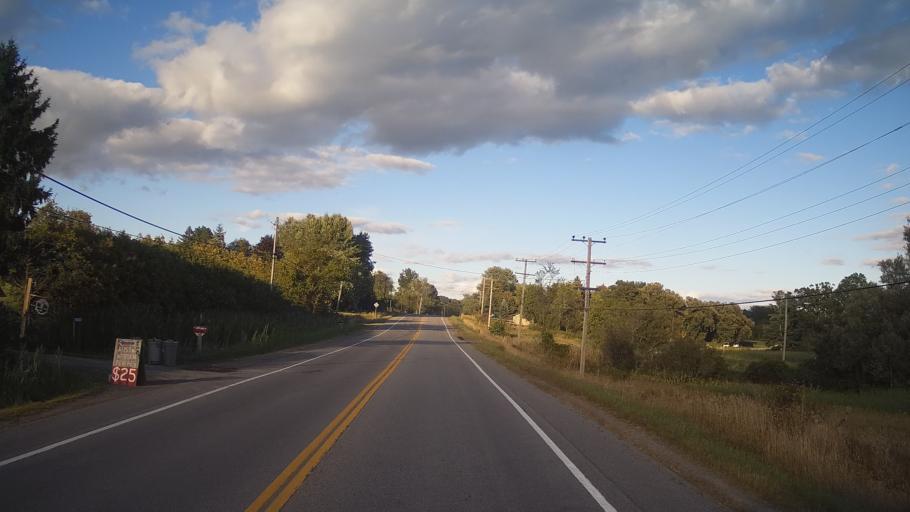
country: CA
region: Ontario
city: Gananoque
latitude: 44.3206
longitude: -76.2293
